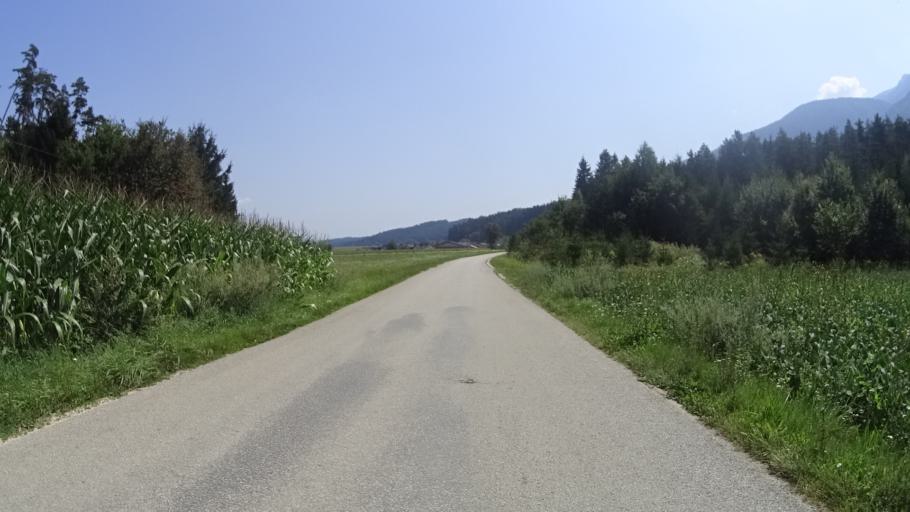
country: AT
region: Carinthia
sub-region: Politischer Bezirk Volkermarkt
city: Globasnitz
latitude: 46.5568
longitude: 14.7155
